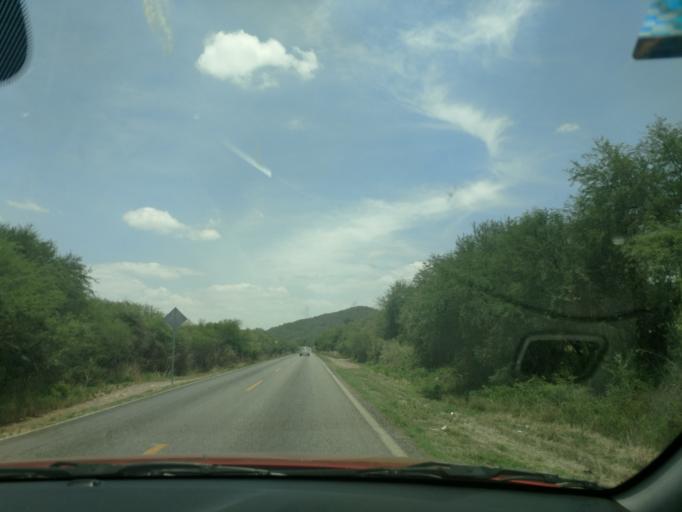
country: MX
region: San Luis Potosi
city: Ciudad Fernandez
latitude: 21.9985
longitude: -100.1406
